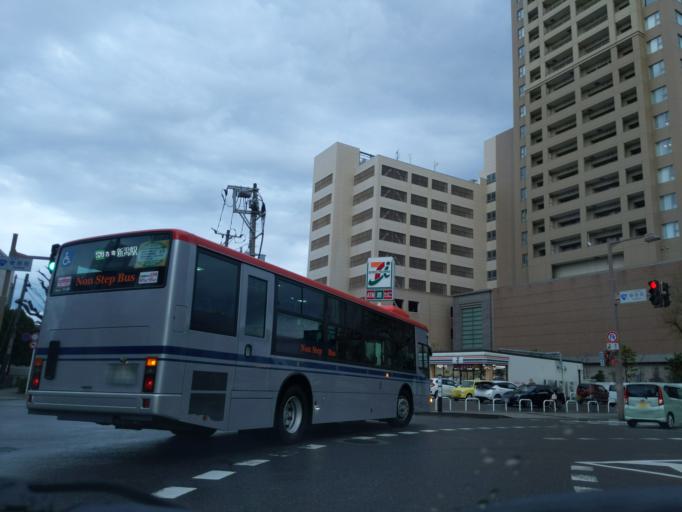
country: JP
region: Niigata
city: Niigata-shi
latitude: 37.9225
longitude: 139.0411
